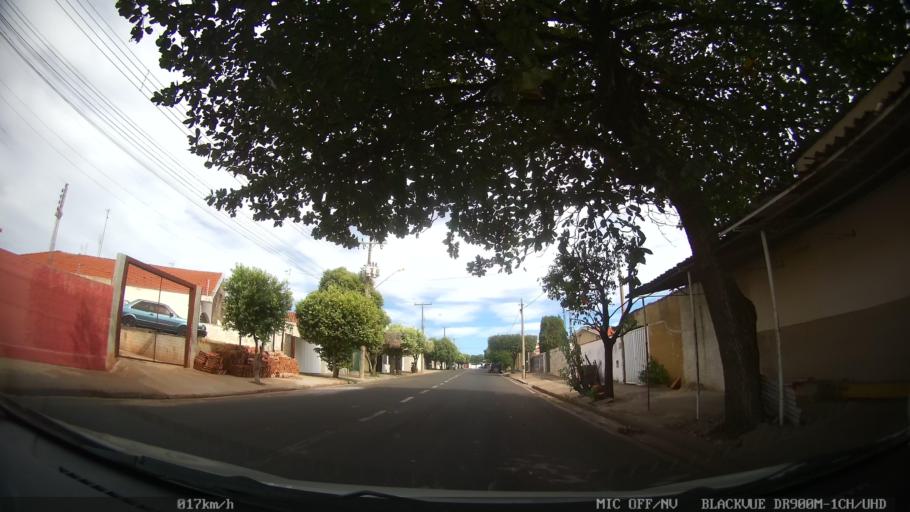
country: BR
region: Sao Paulo
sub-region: Catanduva
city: Catanduva
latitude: -21.1467
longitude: -48.9703
